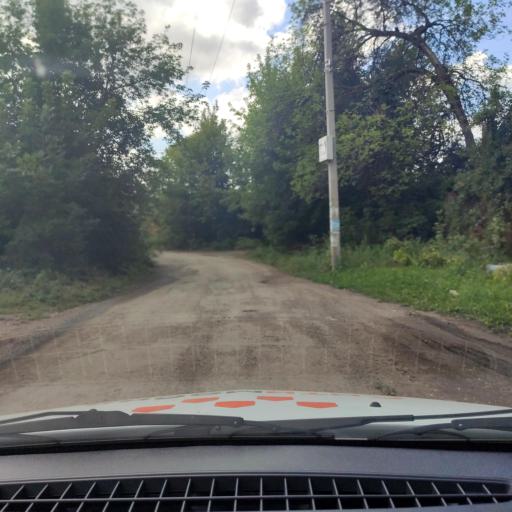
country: RU
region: Bashkortostan
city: Ufa
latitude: 54.7094
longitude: 55.9374
